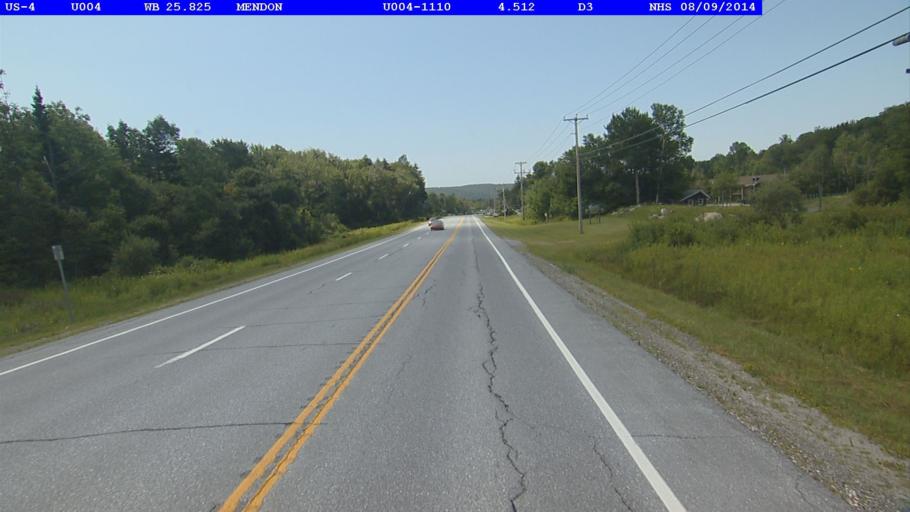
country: US
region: Vermont
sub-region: Rutland County
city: Rutland
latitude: 43.6595
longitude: -72.8691
